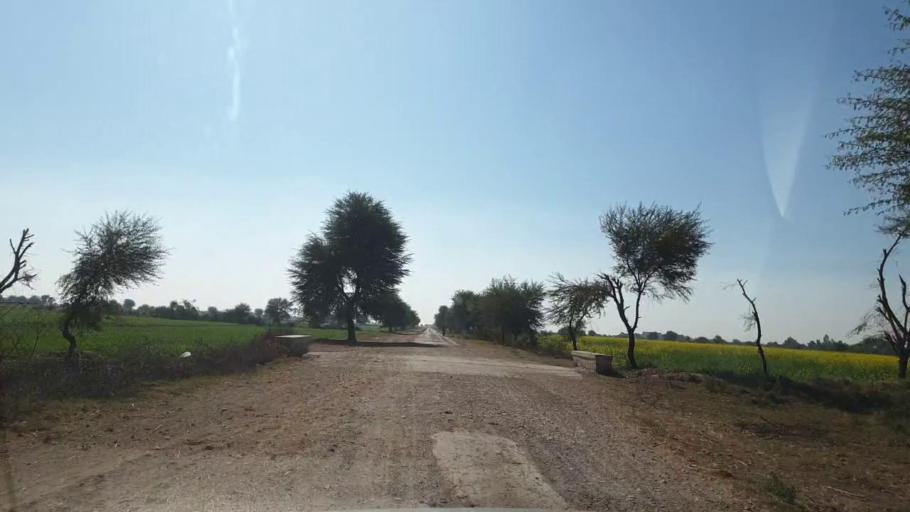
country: PK
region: Sindh
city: Jhol
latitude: 25.8152
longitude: 69.0358
